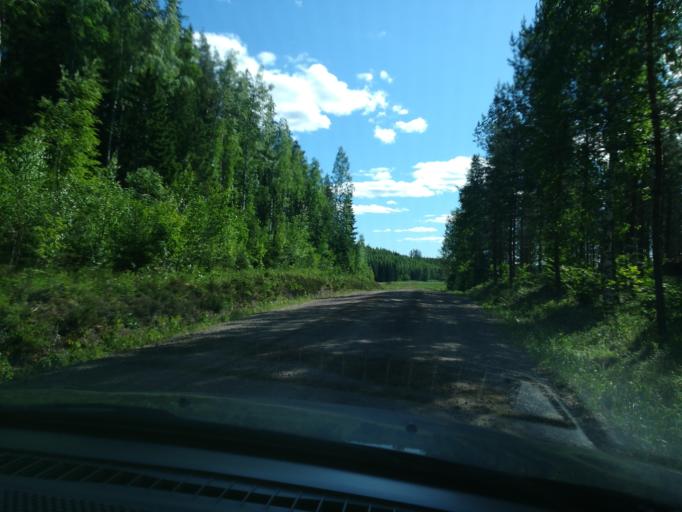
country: FI
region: Southern Savonia
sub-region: Mikkeli
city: Puumala
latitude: 61.6524
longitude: 28.1079
